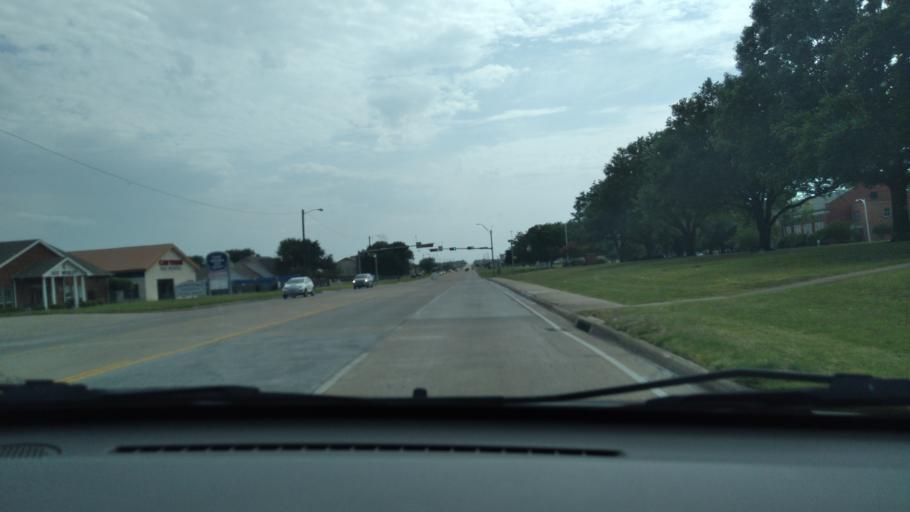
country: US
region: Texas
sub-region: Navarro County
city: Corsicana
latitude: 32.0747
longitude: -96.4980
